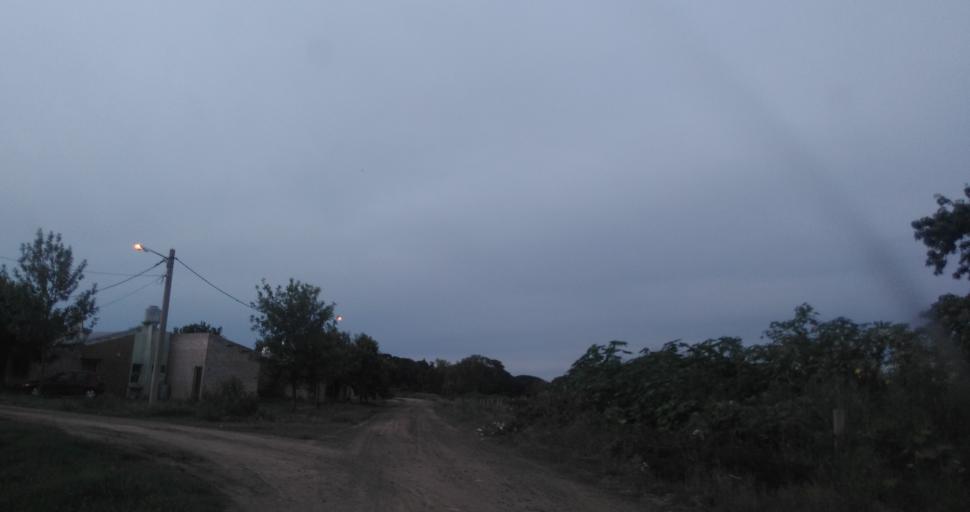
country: AR
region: Chaco
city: Fontana
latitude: -27.4121
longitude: -59.0251
